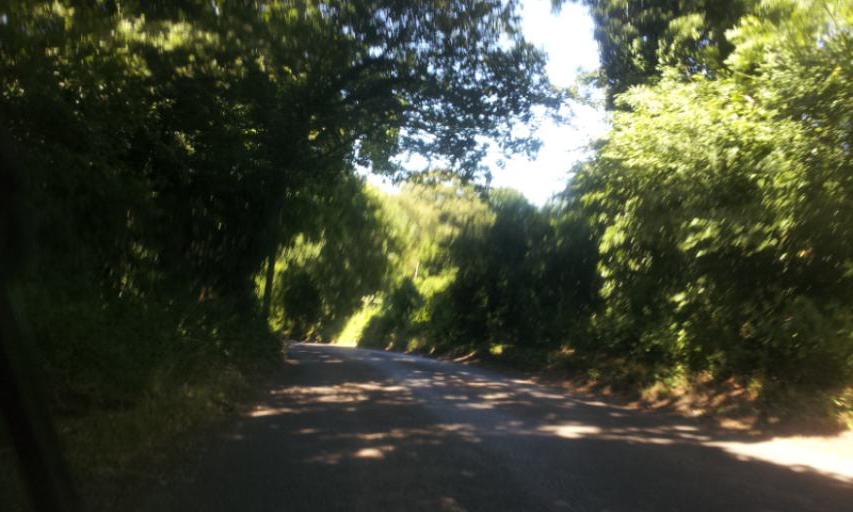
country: GB
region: England
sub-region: Kent
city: Sittingbourne
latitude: 51.3083
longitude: 0.7403
